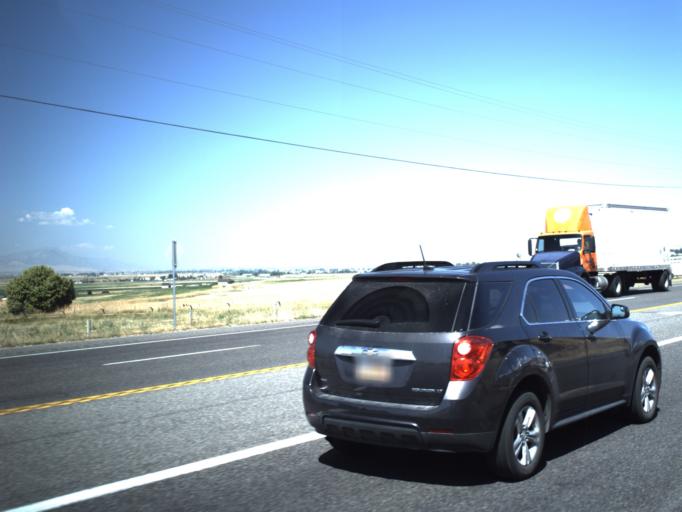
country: US
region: Utah
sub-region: Cache County
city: Richmond
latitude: 41.8870
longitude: -111.8169
